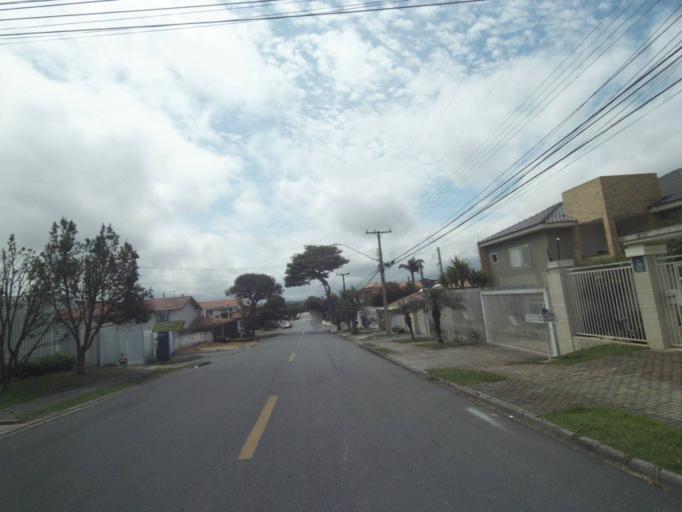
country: BR
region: Parana
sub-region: Pinhais
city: Pinhais
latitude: -25.4332
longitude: -49.2248
